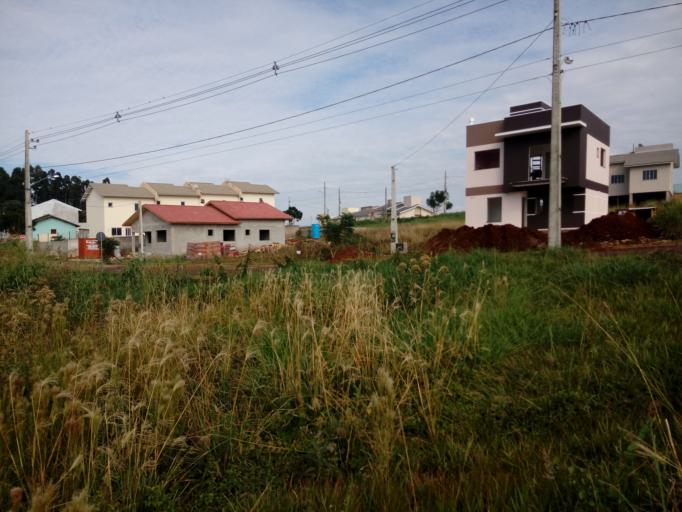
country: BR
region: Santa Catarina
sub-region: Chapeco
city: Chapeco
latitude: -27.0903
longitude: -52.7115
